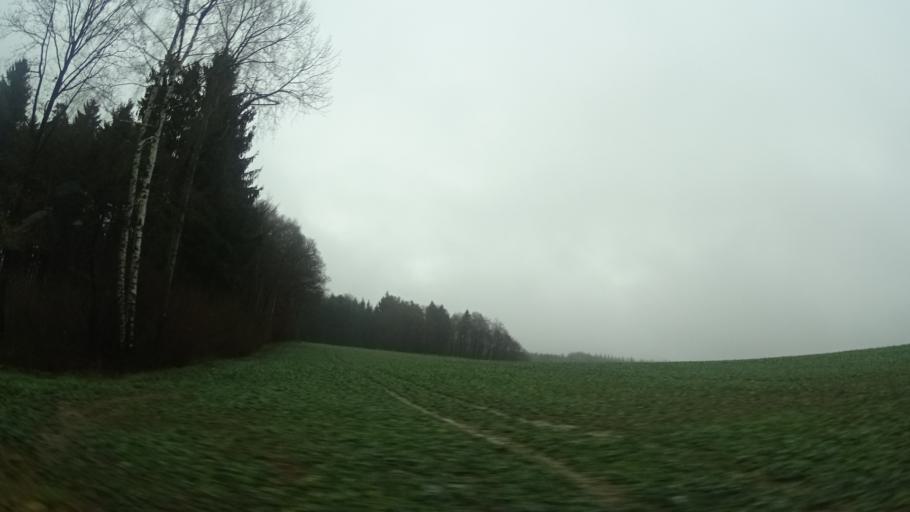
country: DE
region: Hesse
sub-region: Regierungsbezirk Kassel
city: Dipperz
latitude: 50.5340
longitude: 9.8444
